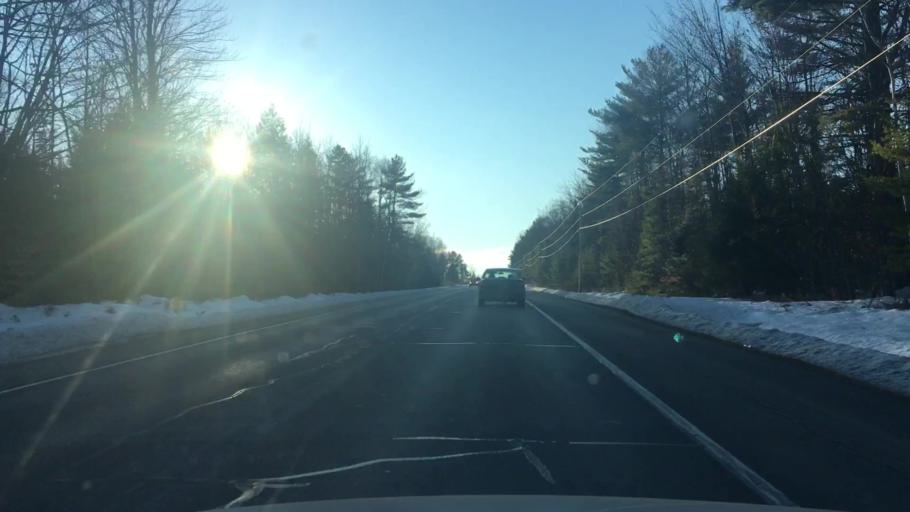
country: US
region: Maine
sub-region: Franklin County
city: New Sharon
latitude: 44.6403
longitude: -69.9923
